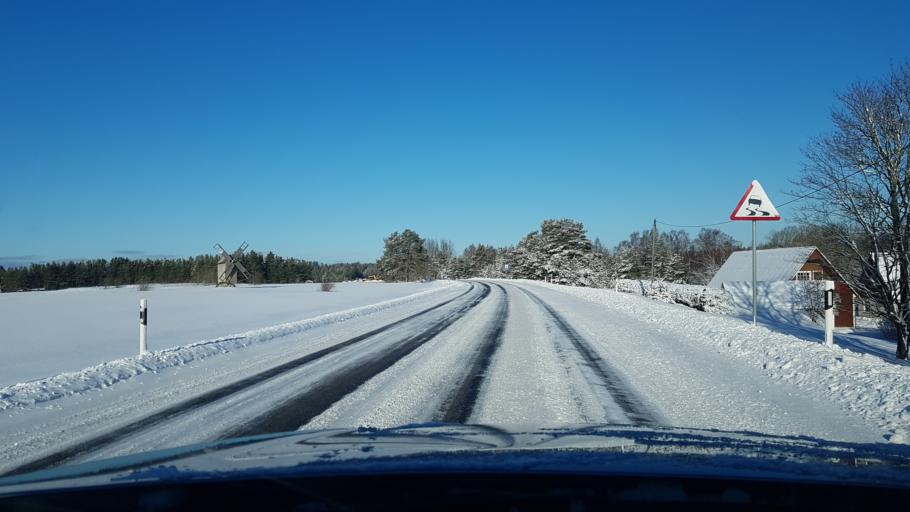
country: EE
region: Hiiumaa
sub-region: Kaerdla linn
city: Kardla
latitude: 58.9564
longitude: 22.7733
